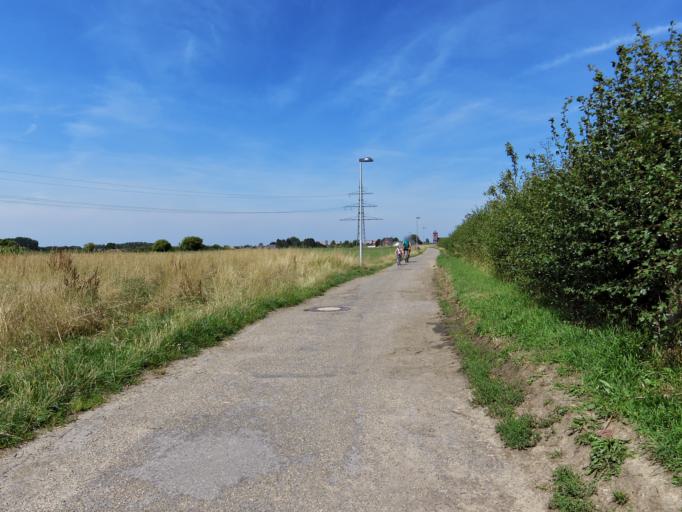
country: NL
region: Limburg
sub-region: Gemeente Kerkrade
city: Kerkrade
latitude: 50.8409
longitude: 6.0707
